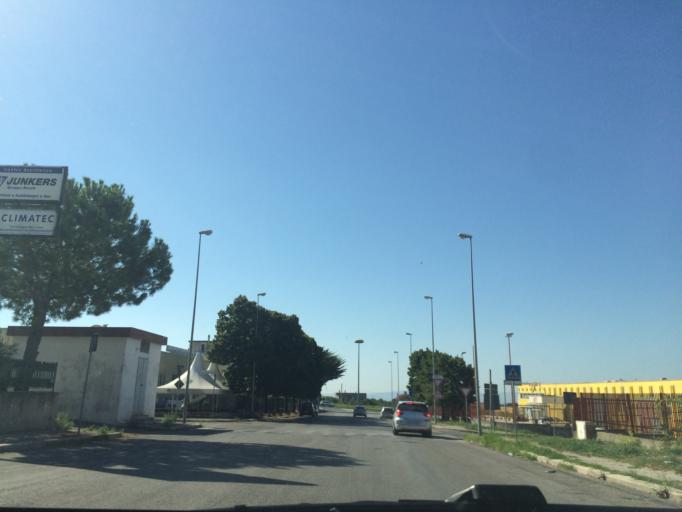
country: IT
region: Basilicate
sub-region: Provincia di Matera
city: Matera
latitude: 40.6706
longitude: 16.5734
